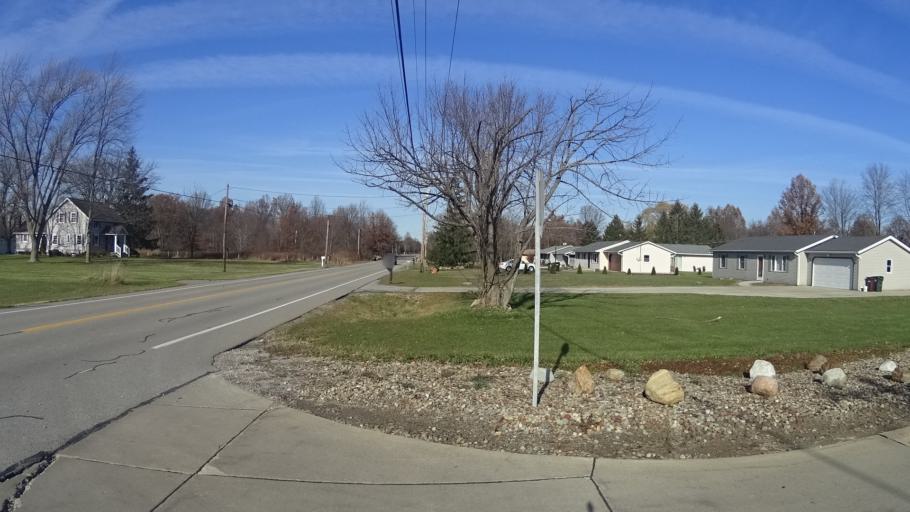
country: US
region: Ohio
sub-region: Lorain County
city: Eaton Estates
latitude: 41.2855
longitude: -81.9818
